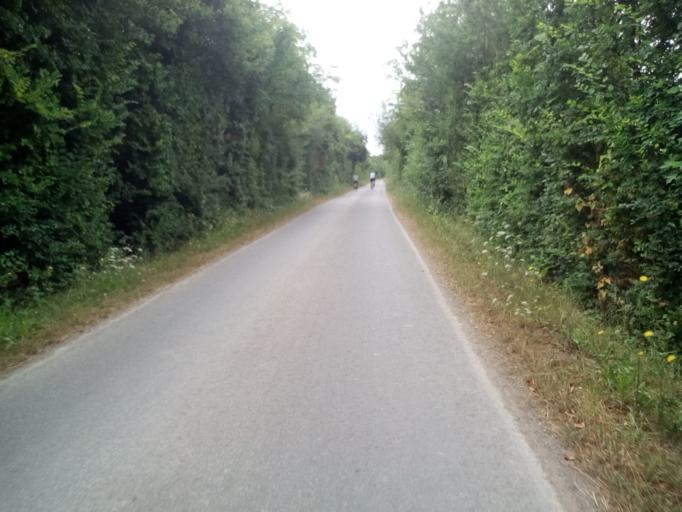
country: FR
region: Lower Normandy
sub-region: Departement du Calvados
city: Cabourg
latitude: 49.2608
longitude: -0.1322
